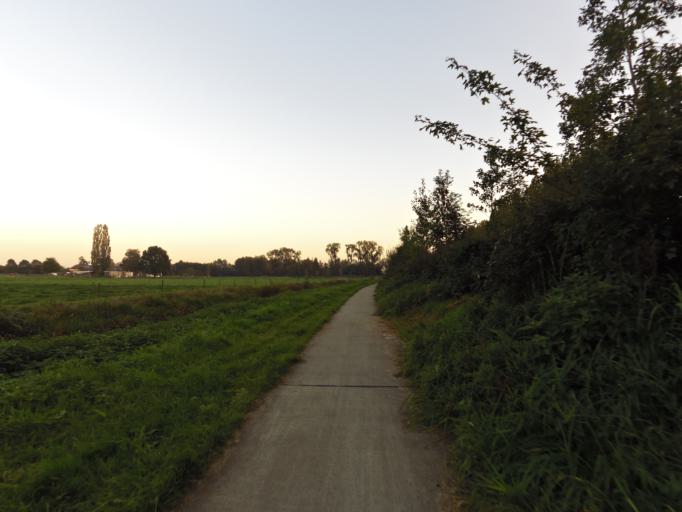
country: NL
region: Gelderland
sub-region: Gemeente Doetinchem
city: Doetinchem
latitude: 51.9280
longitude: 6.3298
